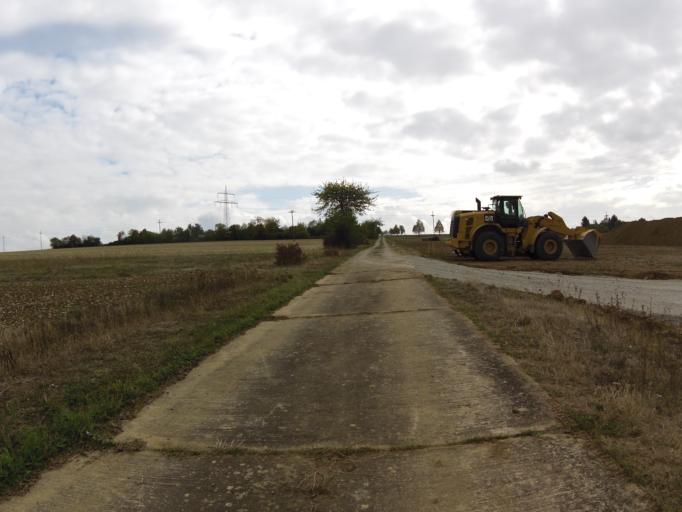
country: DE
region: Bavaria
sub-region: Regierungsbezirk Unterfranken
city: Waldbrunn
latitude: 49.7617
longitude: 9.8099
